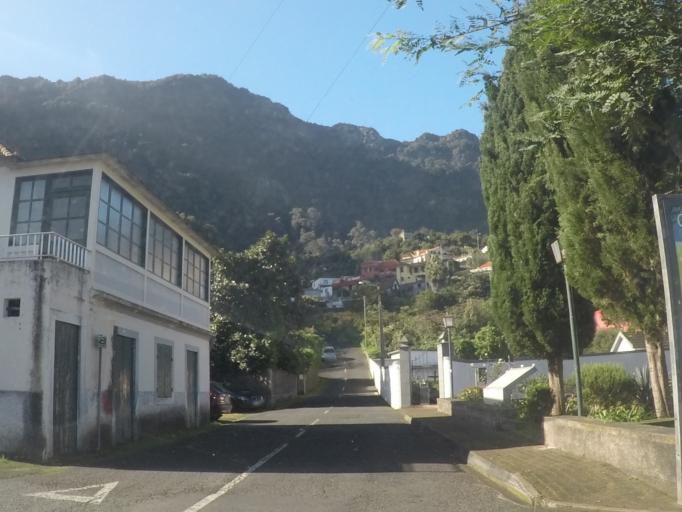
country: PT
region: Madeira
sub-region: Santana
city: Santana
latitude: 32.8266
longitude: -16.9563
